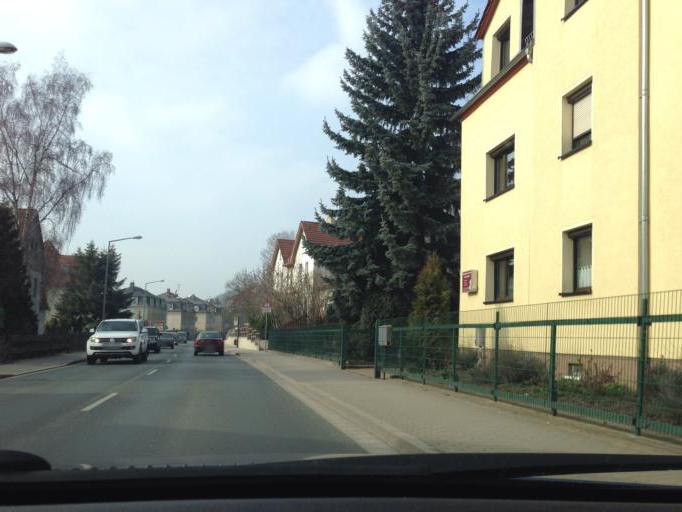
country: DE
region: Saxony
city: Freital
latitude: 51.0224
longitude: 13.6259
